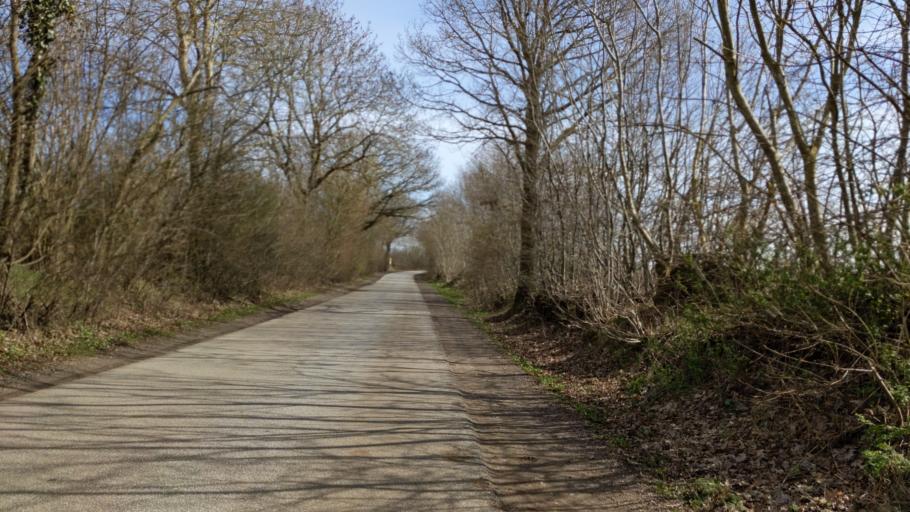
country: DE
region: Schleswig-Holstein
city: Susel
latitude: 54.0722
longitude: 10.6725
